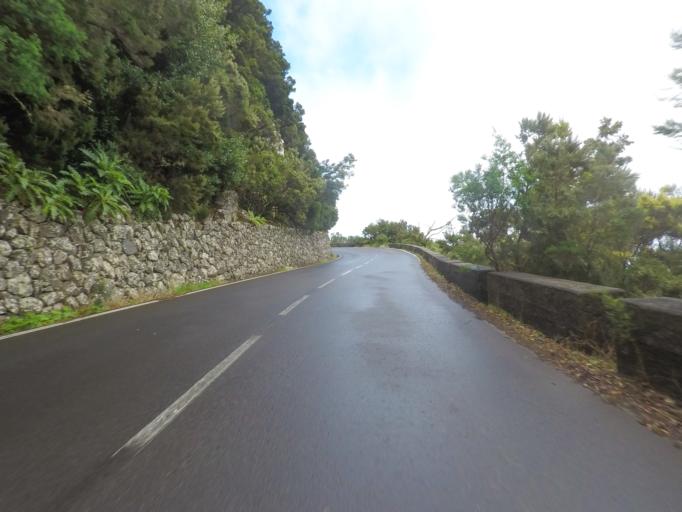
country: ES
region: Canary Islands
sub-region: Provincia de Santa Cruz de Tenerife
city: Vallehermosa
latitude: 28.1617
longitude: -17.2936
